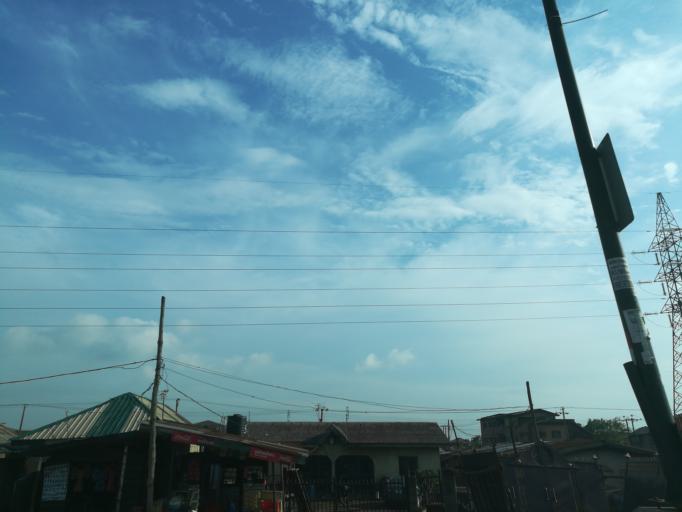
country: NG
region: Lagos
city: Ojota
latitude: 6.6087
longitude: 3.4243
